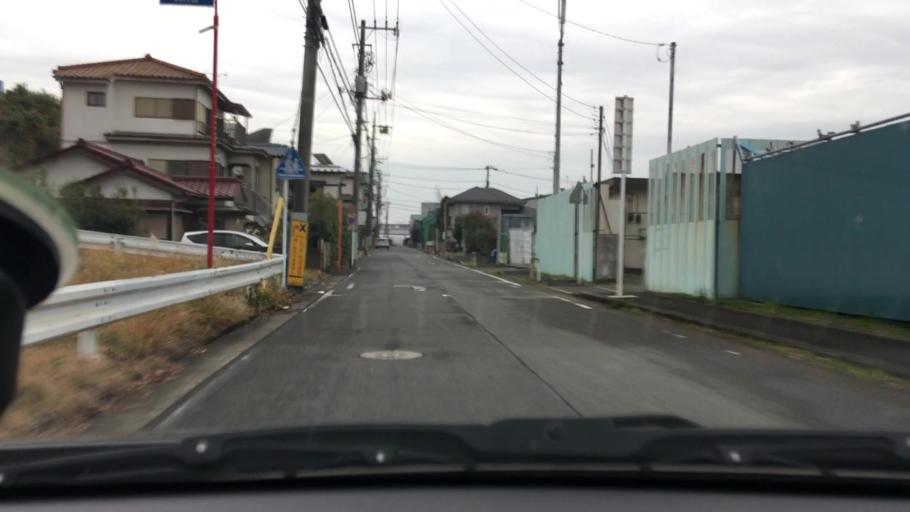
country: JP
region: Kanagawa
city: Yokohama
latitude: 35.5192
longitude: 139.6043
